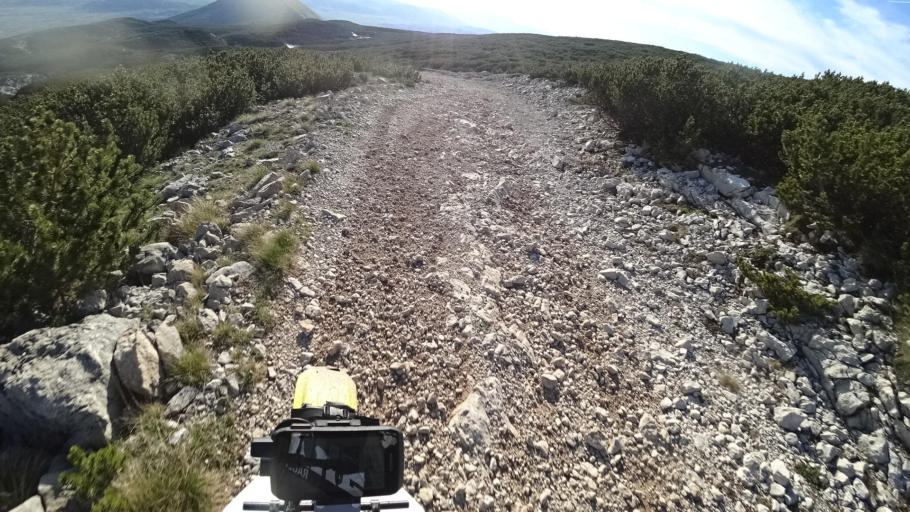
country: BA
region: Federation of Bosnia and Herzegovina
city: Kocerin
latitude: 43.5945
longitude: 17.5398
